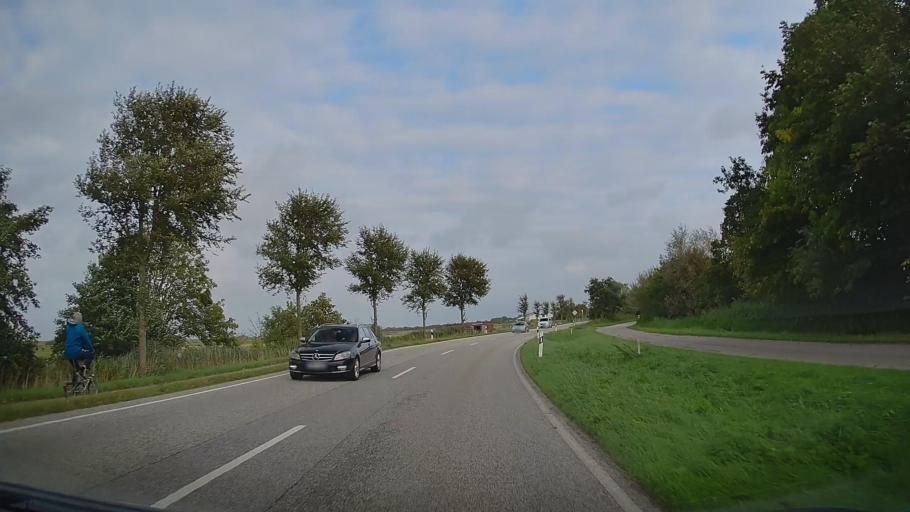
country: DE
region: Schleswig-Holstein
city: Sankt Peter-Ording
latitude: 54.3322
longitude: 8.6286
